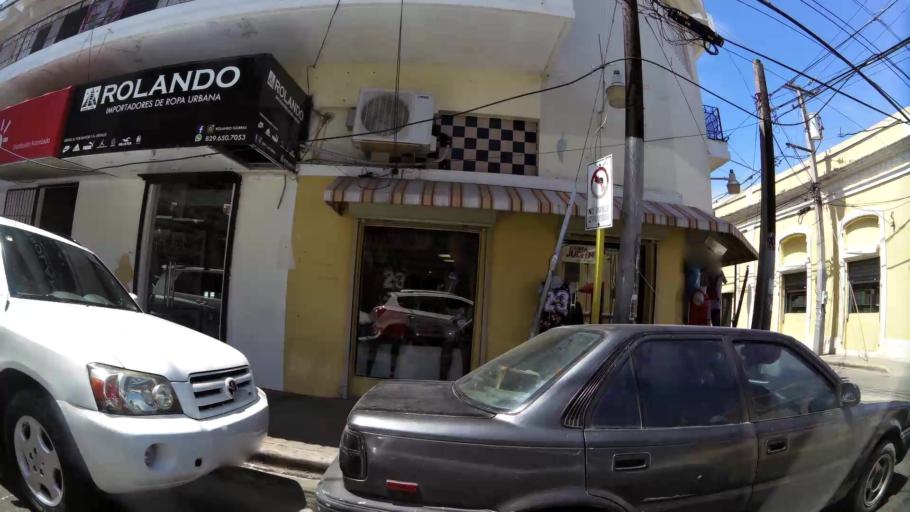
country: DO
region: Santiago
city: Santiago de los Caballeros
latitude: 19.4502
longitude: -70.7039
